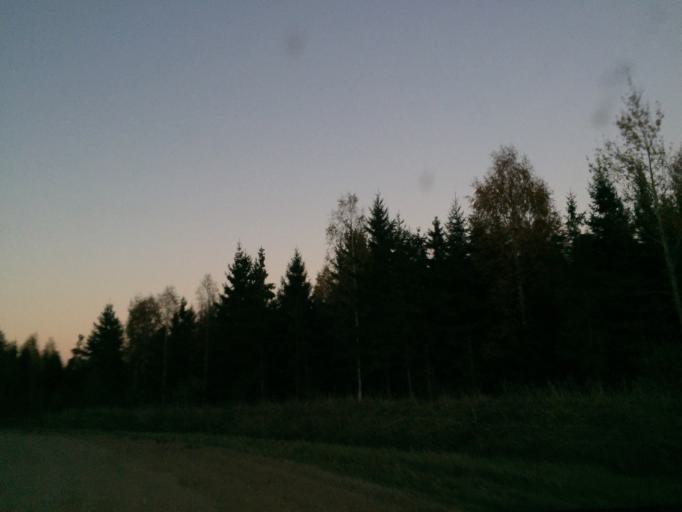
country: LV
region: Auces Novads
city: Auce
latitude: 56.4071
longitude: 22.7989
